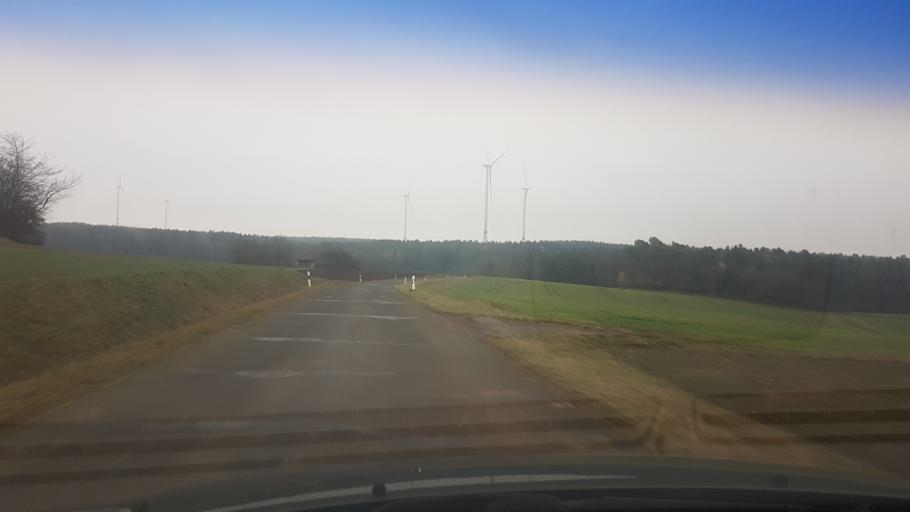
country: DE
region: Bavaria
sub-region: Upper Franconia
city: Weismain
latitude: 50.0586
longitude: 11.2870
